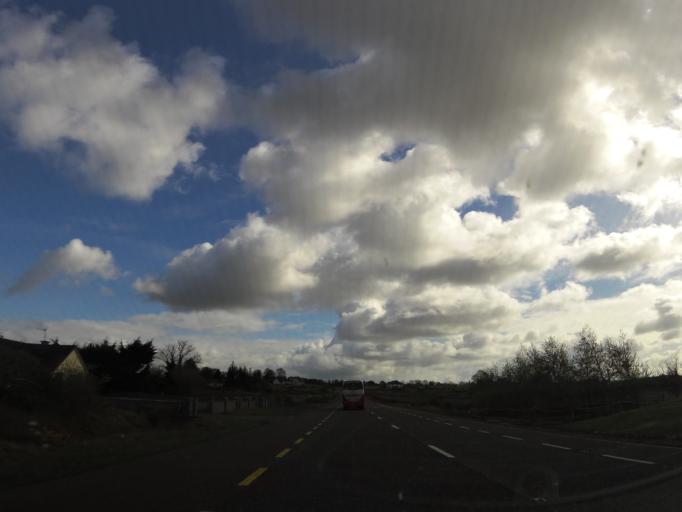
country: IE
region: Connaught
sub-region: Maigh Eo
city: Kiltamagh
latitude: 53.8267
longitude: -8.8773
